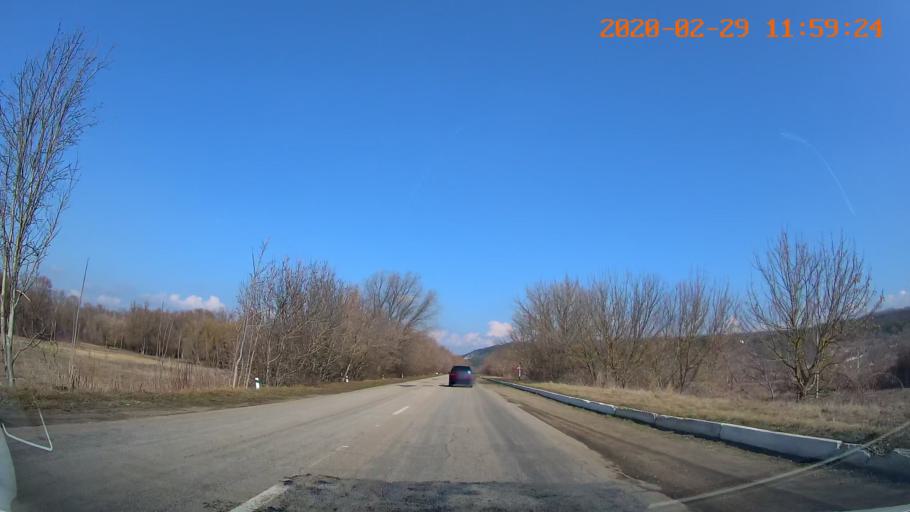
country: MD
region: Telenesti
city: Ribnita
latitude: 47.8247
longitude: 29.0169
